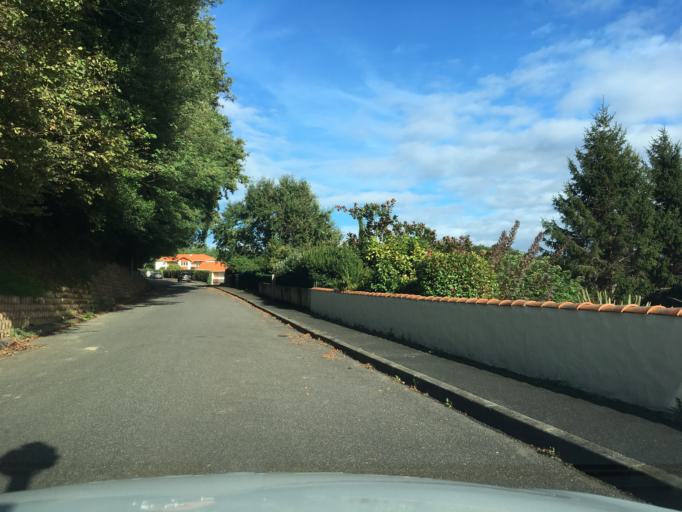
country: FR
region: Aquitaine
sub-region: Departement des Pyrenees-Atlantiques
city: Biarritz
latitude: 43.4600
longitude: -1.5527
